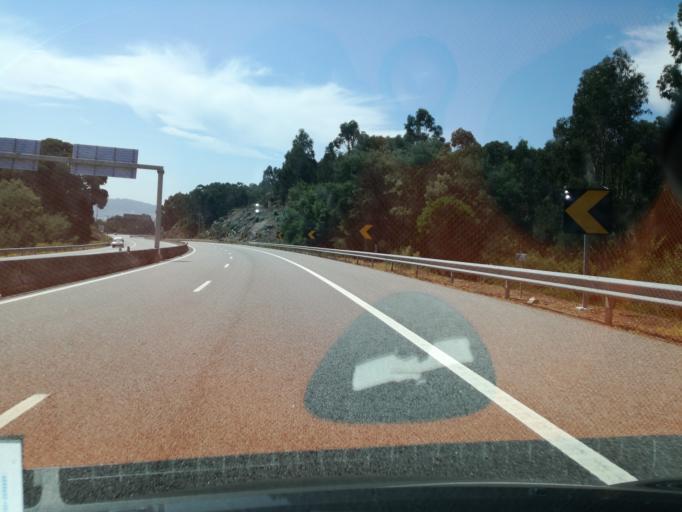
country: PT
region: Viana do Castelo
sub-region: Viana do Castelo
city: Meadela
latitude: 41.7344
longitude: -8.7930
